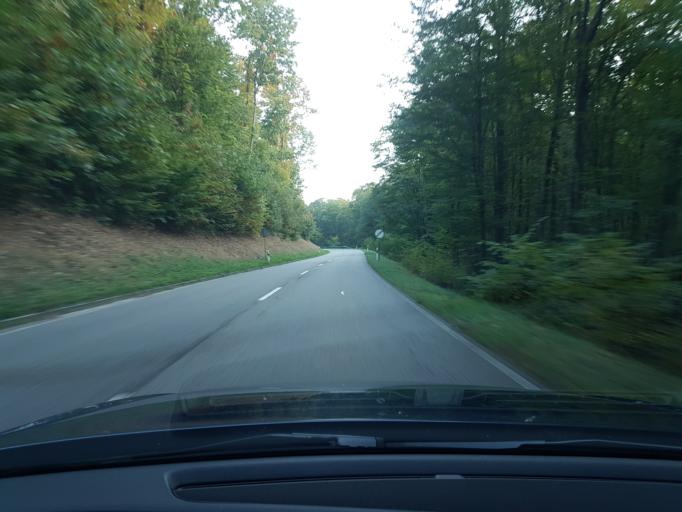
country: DE
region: Hesse
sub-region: Regierungsbezirk Darmstadt
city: Rothenberg
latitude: 49.4999
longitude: 8.9611
